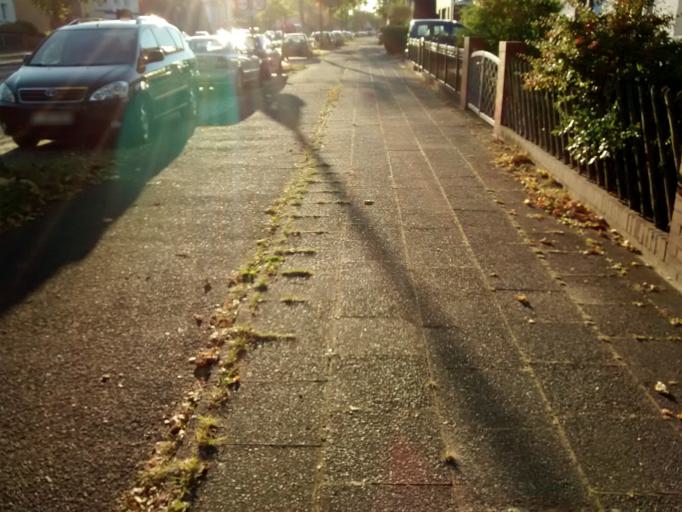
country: DE
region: North Rhine-Westphalia
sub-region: Regierungsbezirk Koln
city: Muelheim
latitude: 50.9969
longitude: 7.0420
